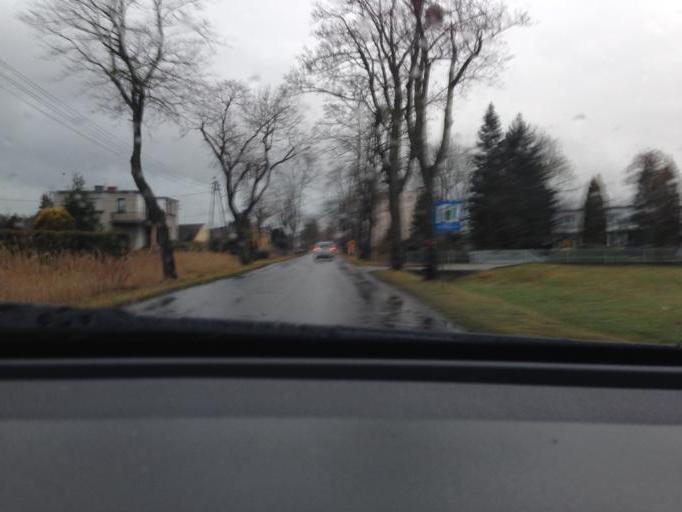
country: PL
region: Opole Voivodeship
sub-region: Powiat opolski
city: Wegry
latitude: 50.7288
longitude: 18.0383
